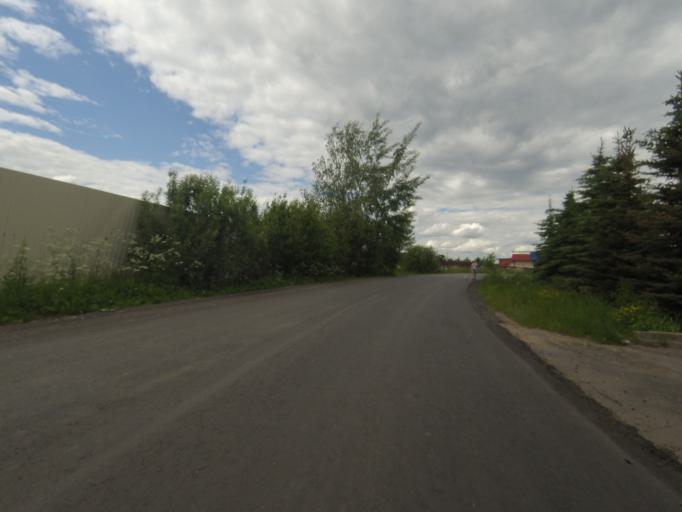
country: RU
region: Moskovskaya
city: Marfino
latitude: 56.0509
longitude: 37.6422
